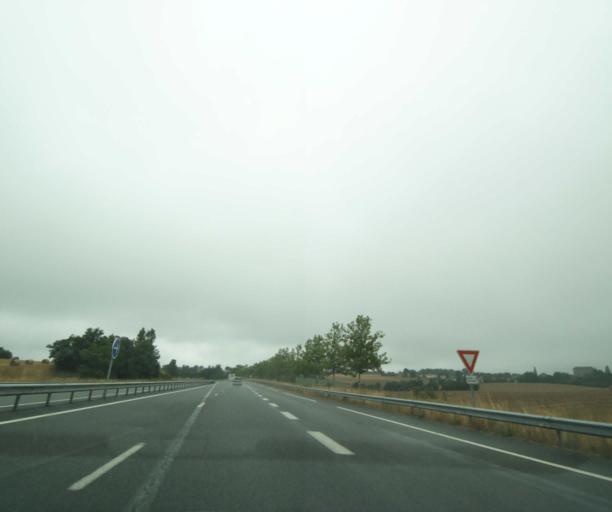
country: FR
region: Midi-Pyrenees
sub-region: Departement de l'Aveyron
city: Naucelle
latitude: 44.1020
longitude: 2.3068
